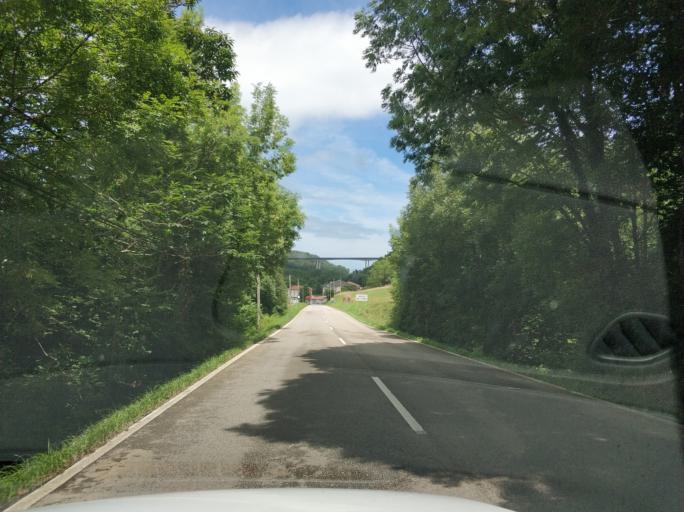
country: ES
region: Asturias
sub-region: Province of Asturias
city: Cudillero
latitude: 43.5555
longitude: -6.2288
